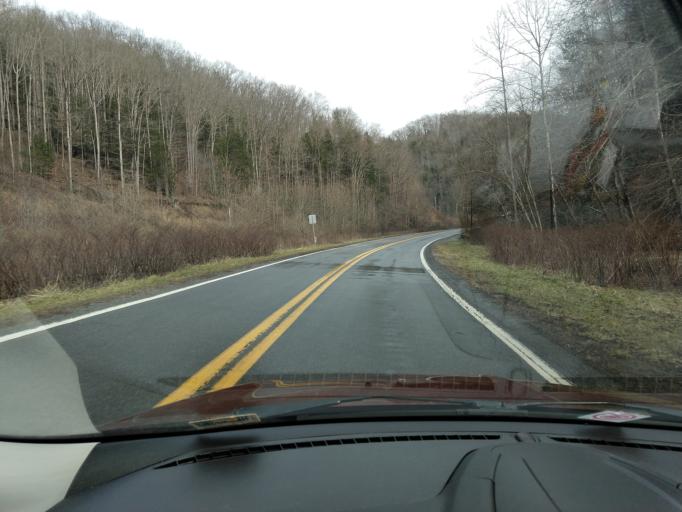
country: US
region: West Virginia
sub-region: McDowell County
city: Welch
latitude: 37.4515
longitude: -81.5428
